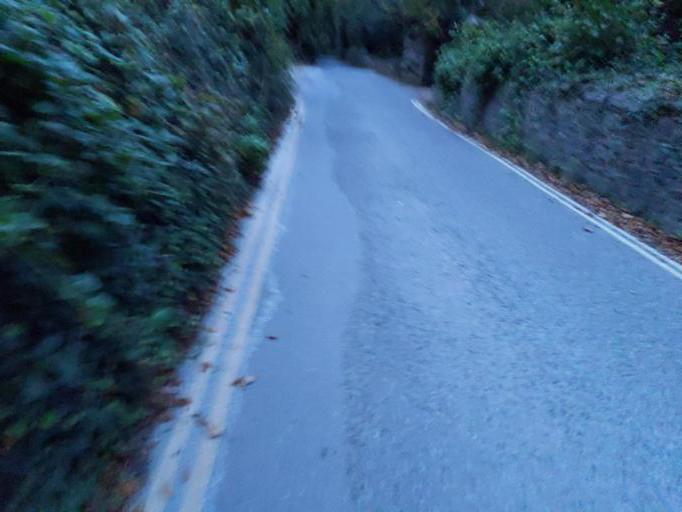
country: GB
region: England
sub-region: Devon
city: Salcombe
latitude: 50.2267
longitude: -3.7840
